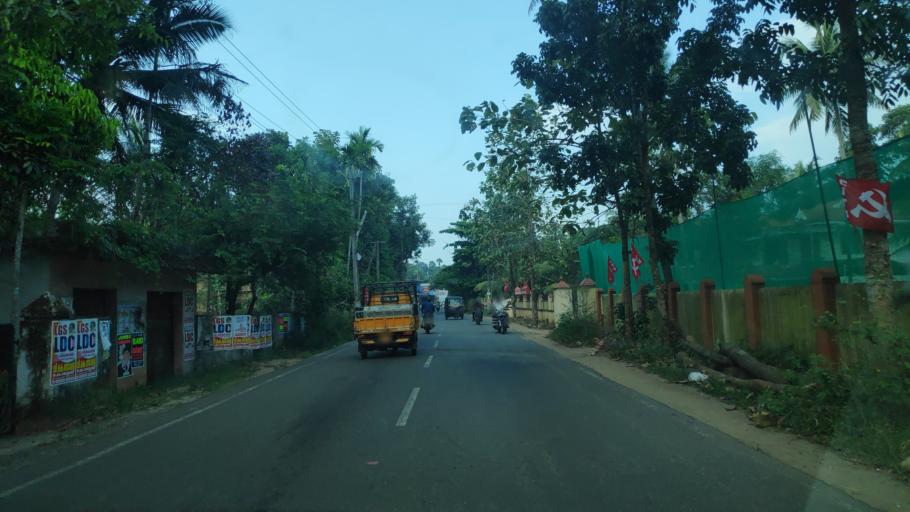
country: IN
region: Kerala
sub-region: Alappuzha
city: Alleppey
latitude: 9.5777
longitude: 76.3490
